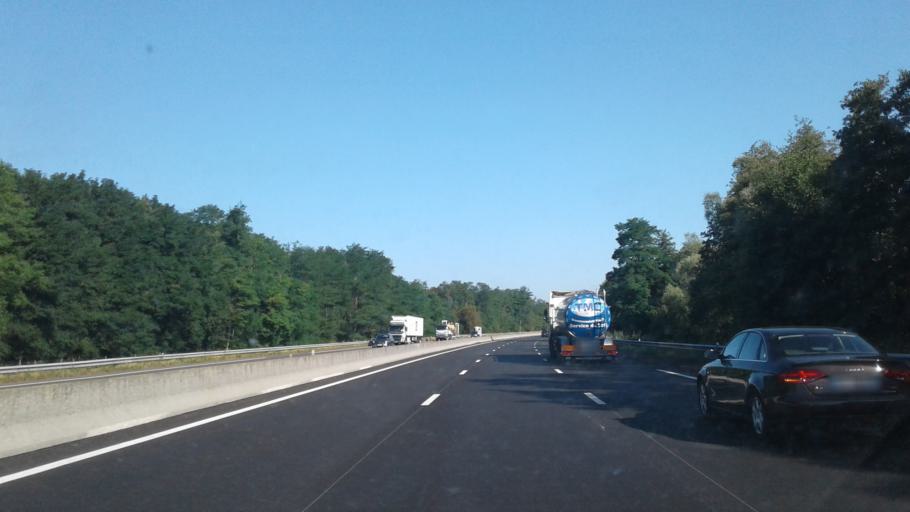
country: FR
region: Rhone-Alpes
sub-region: Departement de l'Ain
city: Certines
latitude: 46.1198
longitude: 5.2865
